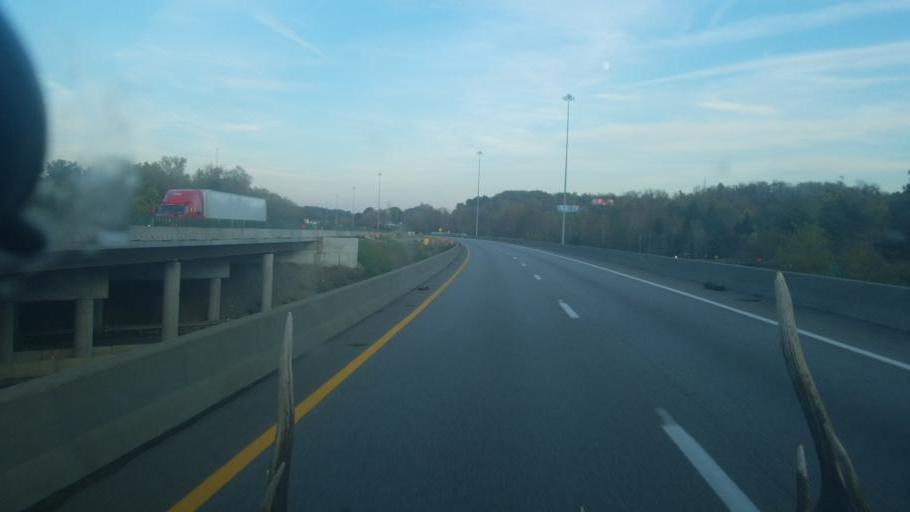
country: US
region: Ohio
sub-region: Muskingum County
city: Zanesville
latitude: 39.9480
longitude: -82.0475
